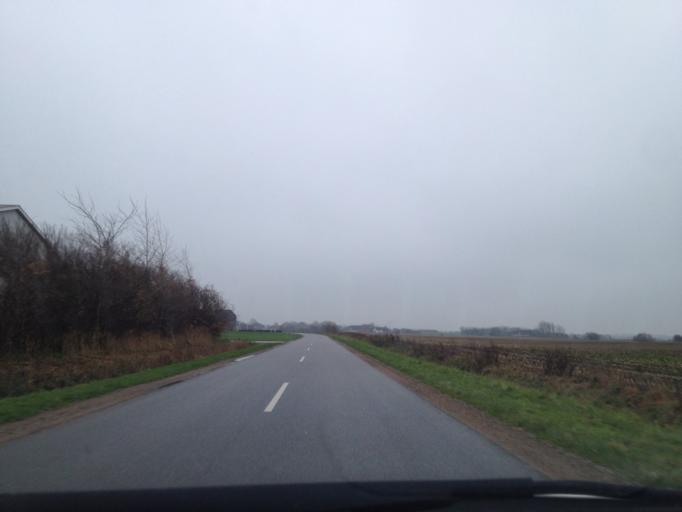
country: DK
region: South Denmark
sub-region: Tonder Kommune
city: Sherrebek
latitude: 55.0944
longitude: 8.7254
